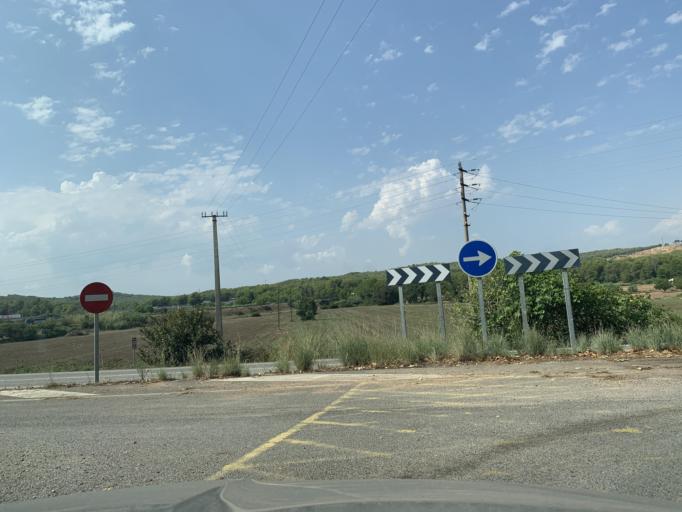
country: ES
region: Catalonia
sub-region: Provincia de Tarragona
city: Altafulla
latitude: 41.1390
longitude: 1.3528
